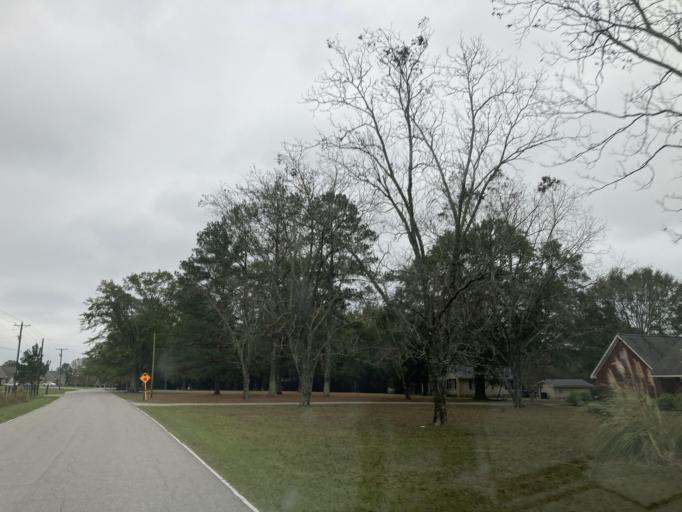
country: US
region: Mississippi
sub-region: Lamar County
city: Purvis
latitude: 31.1500
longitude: -89.4325
